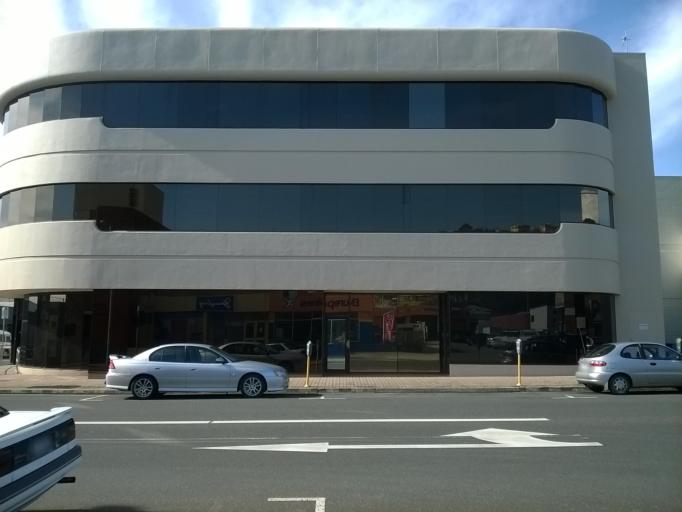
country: AU
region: Tasmania
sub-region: Burnie
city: Burnie
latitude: -41.0523
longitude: 145.9034
